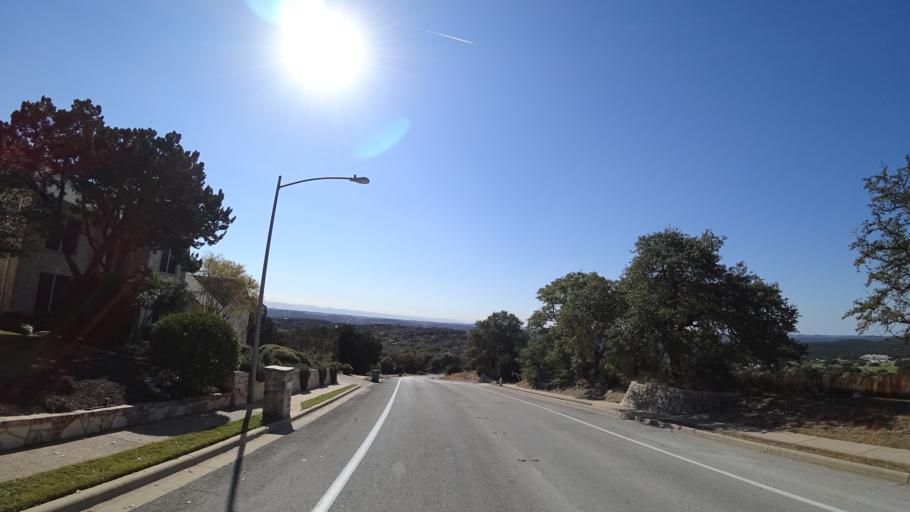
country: US
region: Texas
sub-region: Travis County
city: Lost Creek
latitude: 30.3704
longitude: -97.8461
